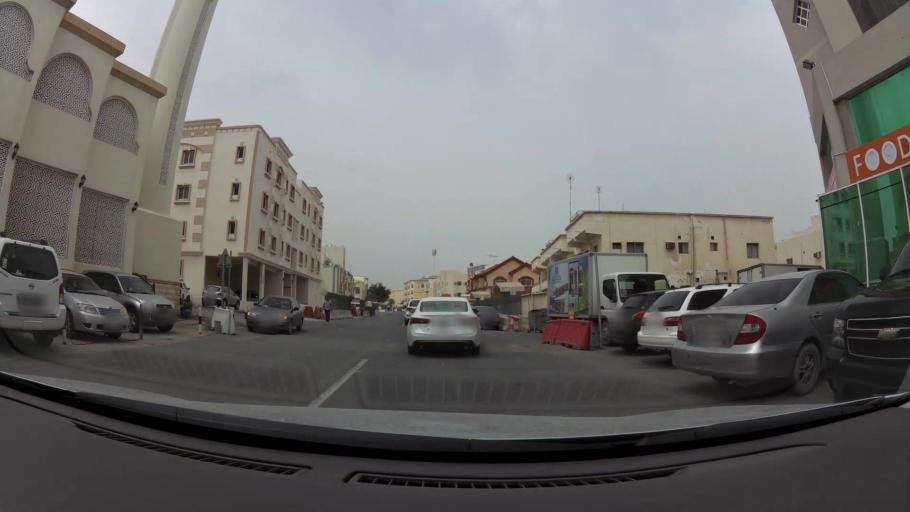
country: QA
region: Baladiyat ad Dawhah
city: Doha
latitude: 25.2530
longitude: 51.5572
